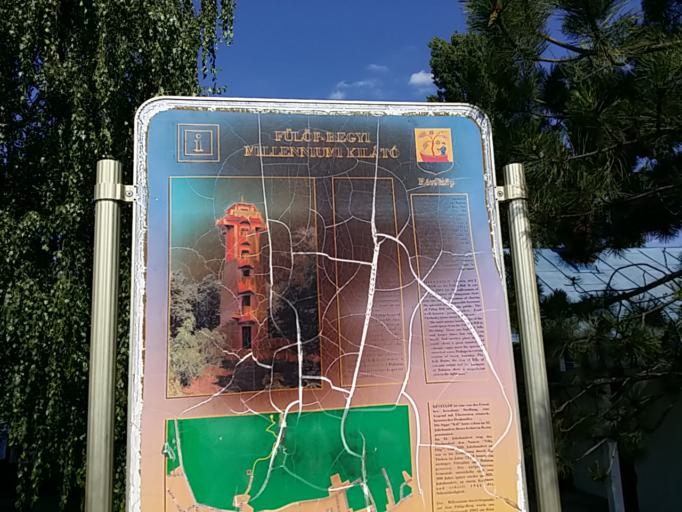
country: HU
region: Somogy
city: Balatonboglar
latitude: 46.7808
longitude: 17.6485
